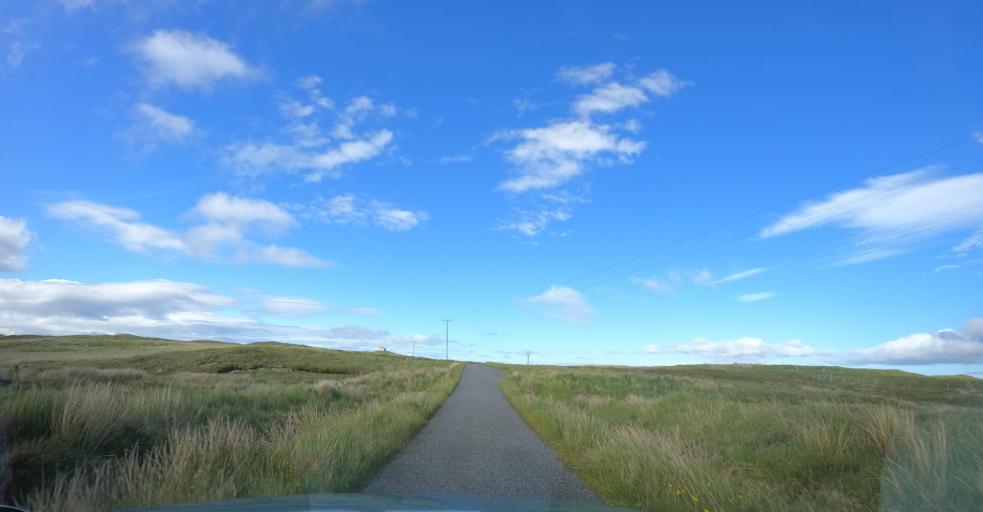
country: GB
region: Scotland
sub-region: Eilean Siar
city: Stornoway
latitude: 58.1755
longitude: -6.5558
